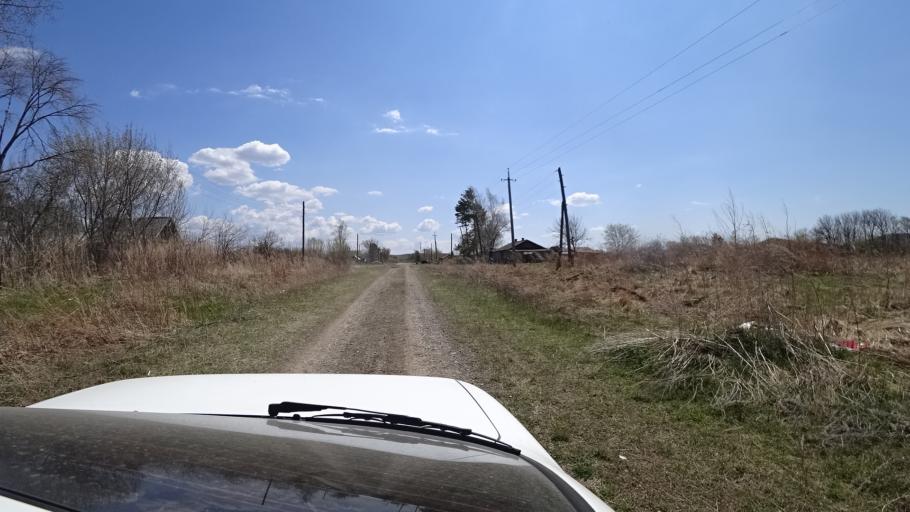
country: RU
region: Primorskiy
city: Lazo
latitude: 45.8025
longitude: 133.7621
